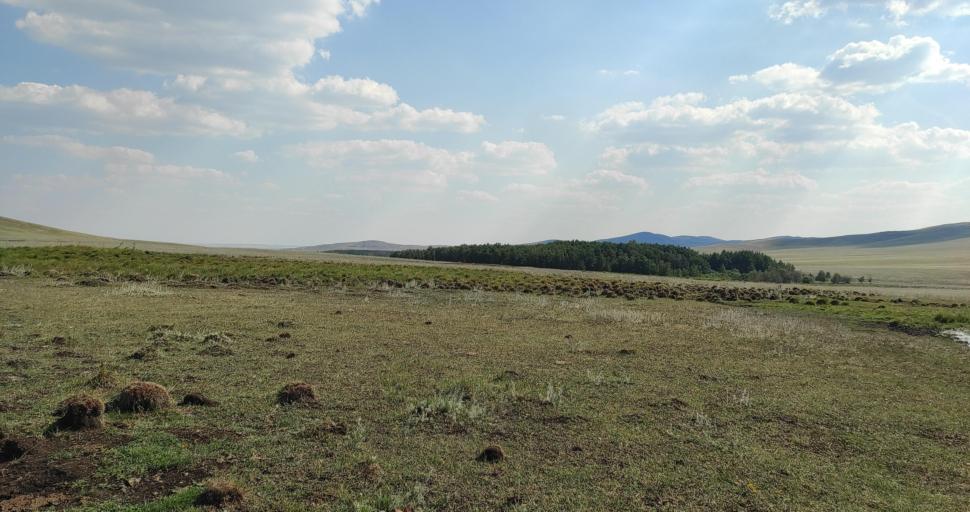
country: RU
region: Bashkortostan
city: Sibay
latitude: 52.5789
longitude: 58.5407
